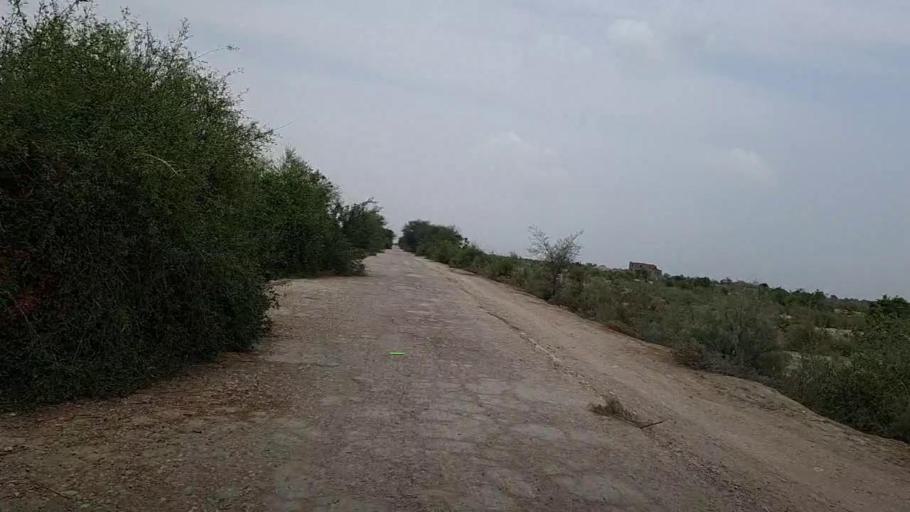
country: PK
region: Sindh
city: Sann
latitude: 26.2030
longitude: 67.9706
